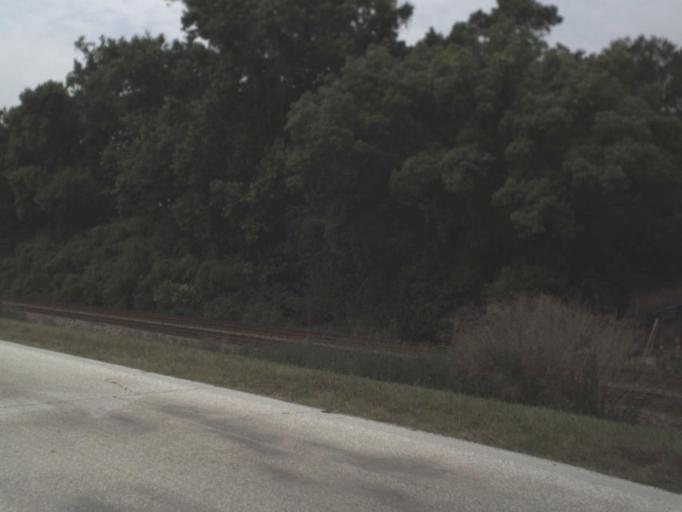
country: US
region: Florida
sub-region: Duval County
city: Jacksonville
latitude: 30.3008
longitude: -81.7205
